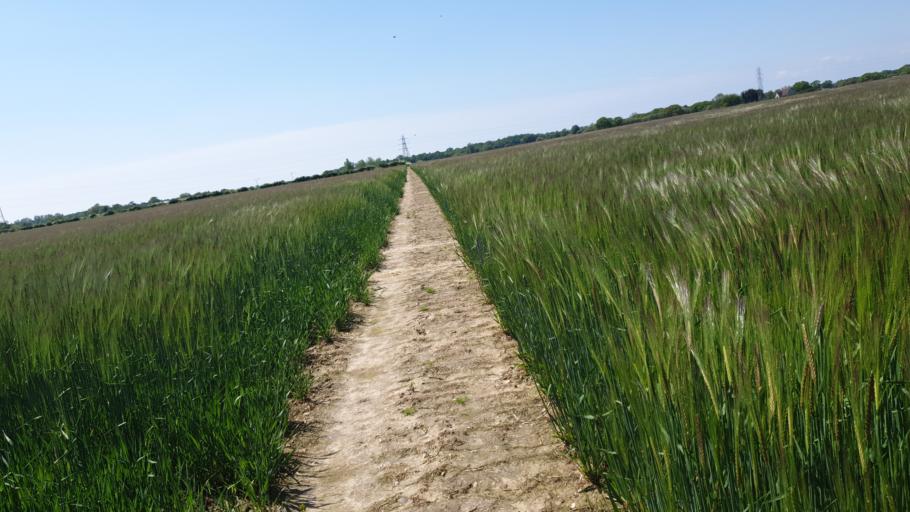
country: GB
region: England
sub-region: Essex
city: Manningtree
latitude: 51.9083
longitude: 1.0420
